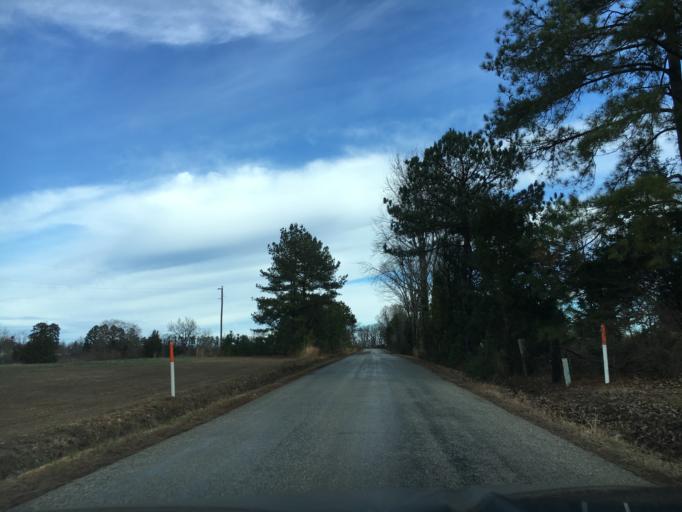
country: US
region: Virginia
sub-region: Nottoway County
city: Crewe
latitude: 37.2414
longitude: -78.2285
